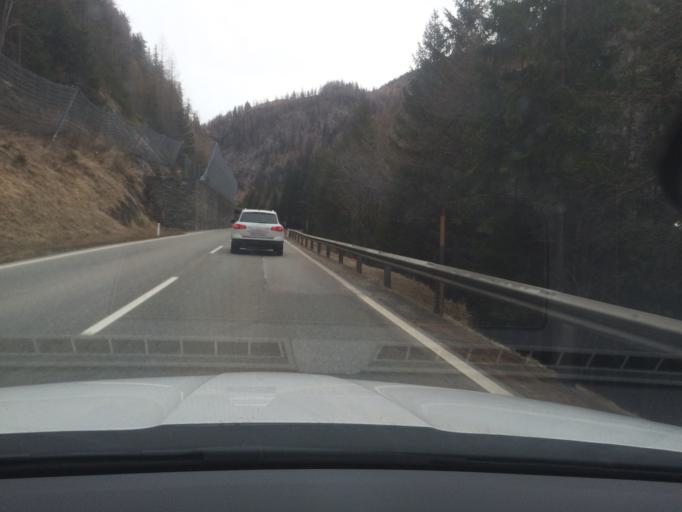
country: AT
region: Tyrol
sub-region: Politischer Bezirk Lienz
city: Matrei in Osttirol
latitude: 47.0323
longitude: 12.5198
